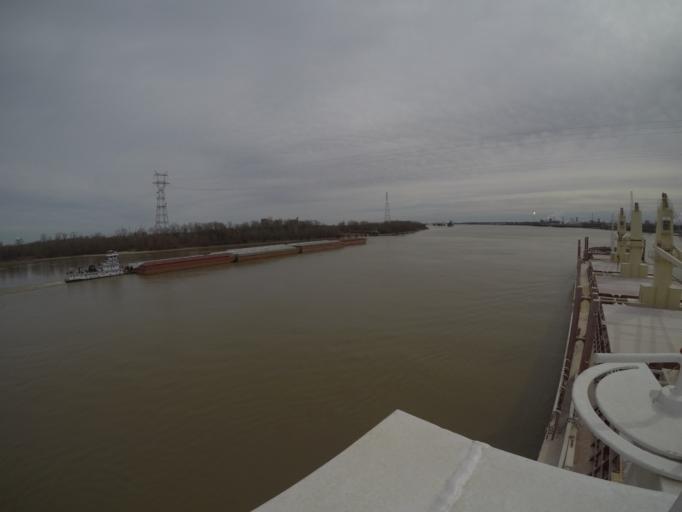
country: US
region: Louisiana
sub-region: Saint Charles Parish
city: Montz
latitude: 30.0018
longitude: -90.4718
